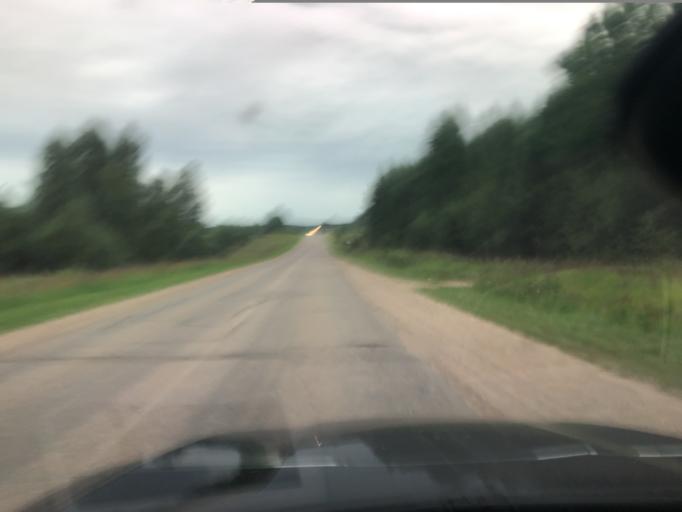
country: RU
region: Jaroslavl
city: Petrovsk
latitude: 56.9878
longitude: 39.1667
